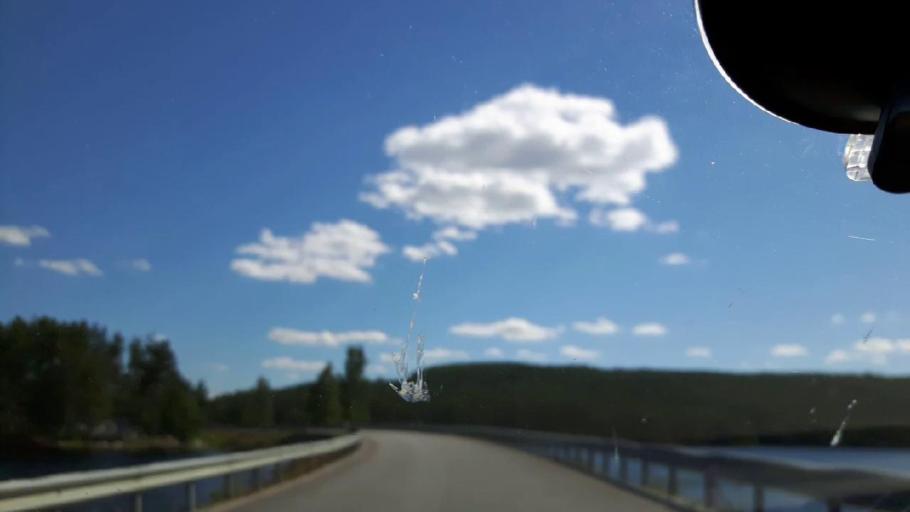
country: SE
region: Vaesternorrland
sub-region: Ange Kommun
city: Fransta
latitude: 62.6943
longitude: 16.3903
